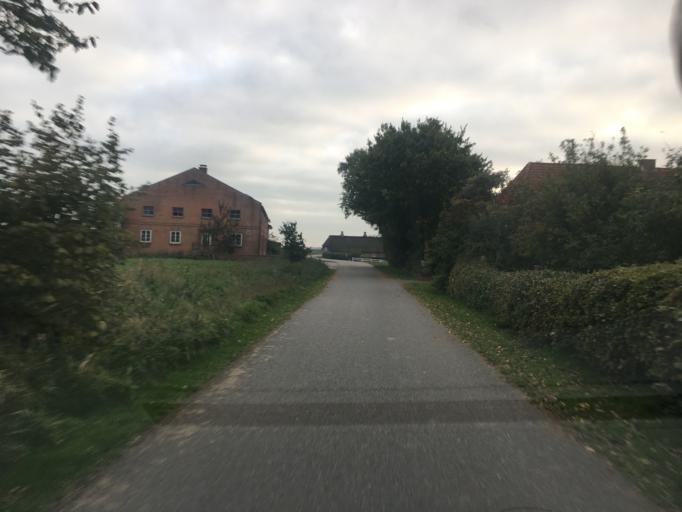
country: DE
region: Schleswig-Holstein
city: Rodenas
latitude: 54.9670
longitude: 8.7373
